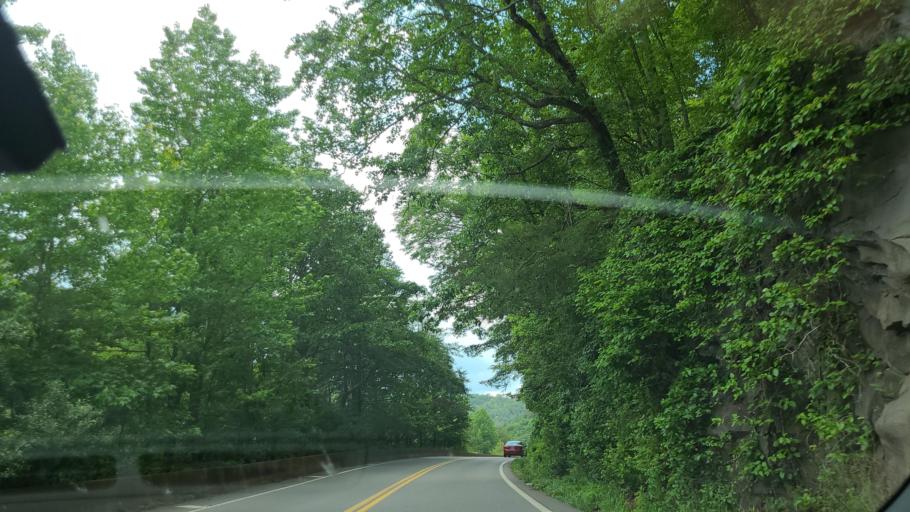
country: US
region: Georgia
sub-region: Fannin County
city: McCaysville
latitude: 35.0694
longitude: -84.4663
